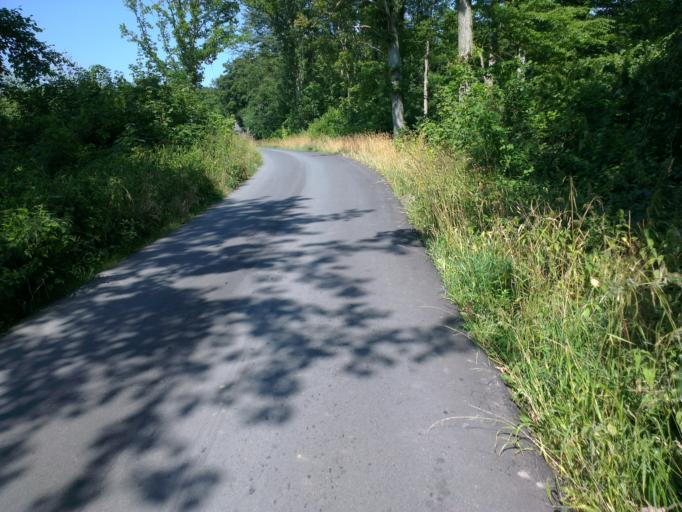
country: DK
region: Capital Region
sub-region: Frederikssund Kommune
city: Jaegerspris
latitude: 55.8766
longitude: 11.9842
